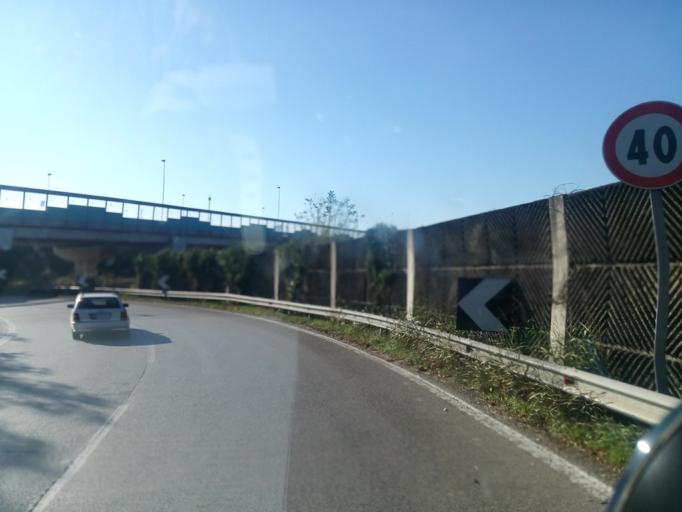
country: IT
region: Veneto
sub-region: Provincia di Padova
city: San Vito
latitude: 45.4315
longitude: 11.9524
